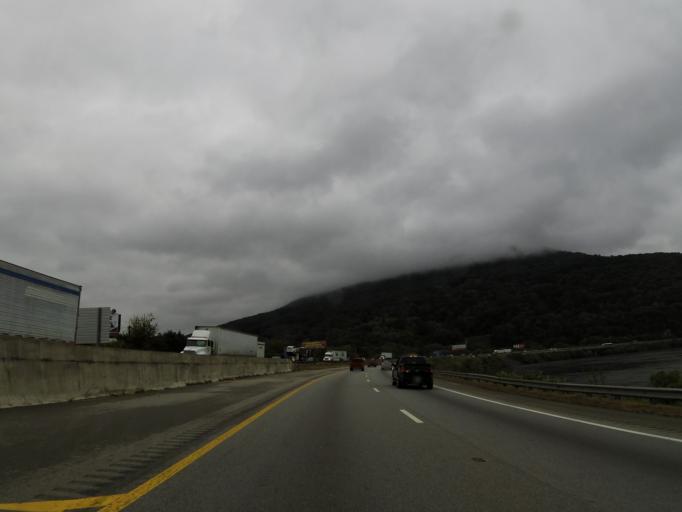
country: US
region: Tennessee
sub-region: Hamilton County
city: Chattanooga
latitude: 35.0217
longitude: -85.3263
